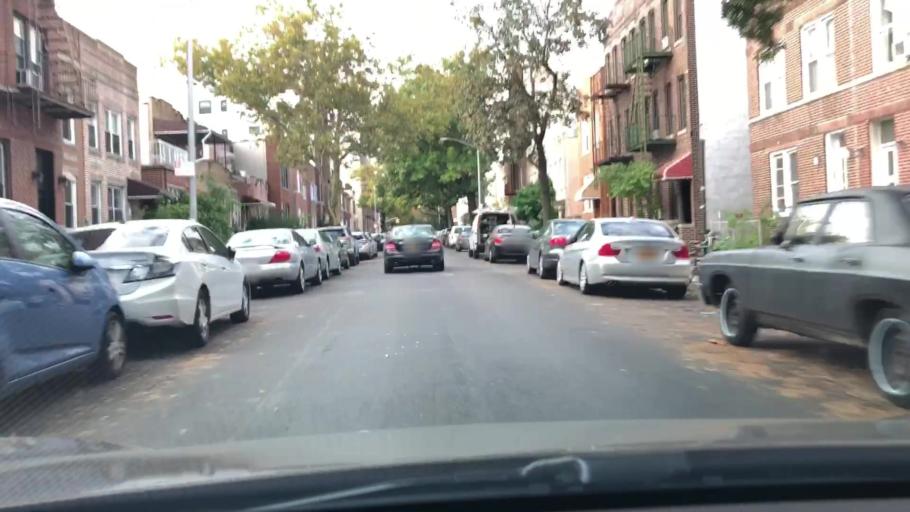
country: US
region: New York
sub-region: Queens County
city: Long Island City
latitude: 40.7690
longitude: -73.9164
